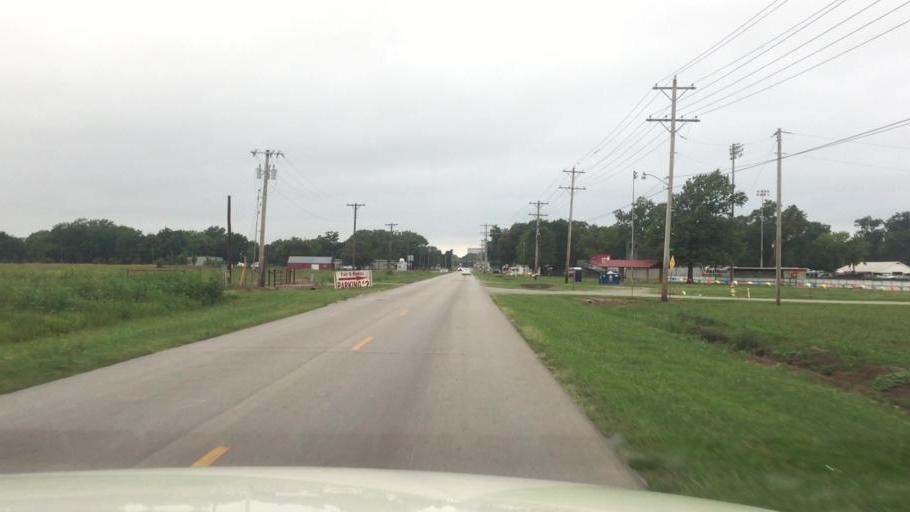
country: US
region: Kansas
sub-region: Montgomery County
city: Coffeyville
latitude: 37.0355
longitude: -95.5906
